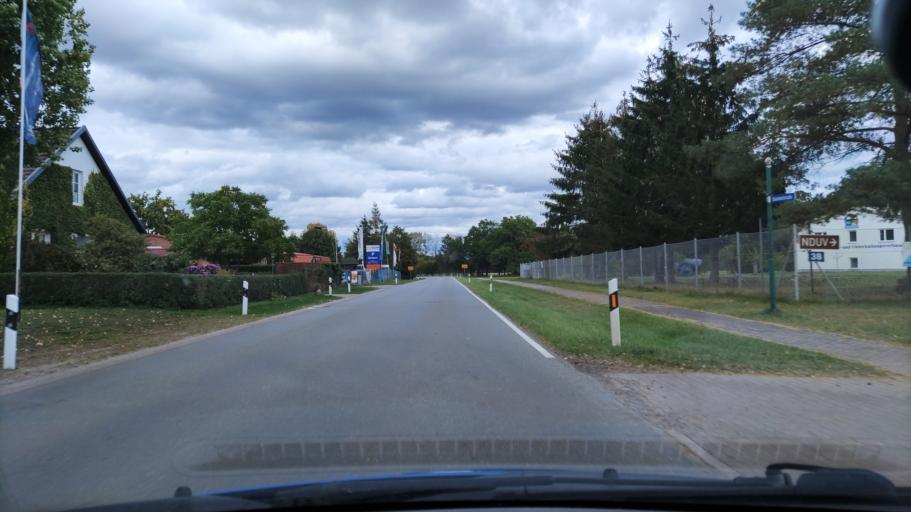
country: DE
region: Lower Saxony
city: Neu Darchau
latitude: 53.2898
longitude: 10.9471
